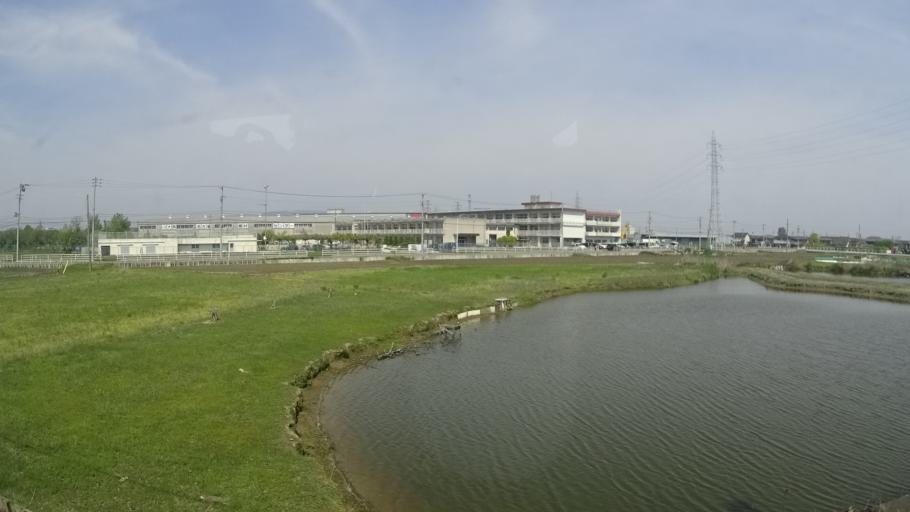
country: JP
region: Aichi
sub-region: Aisai-shi
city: Aisai
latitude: 35.1246
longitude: 136.7487
